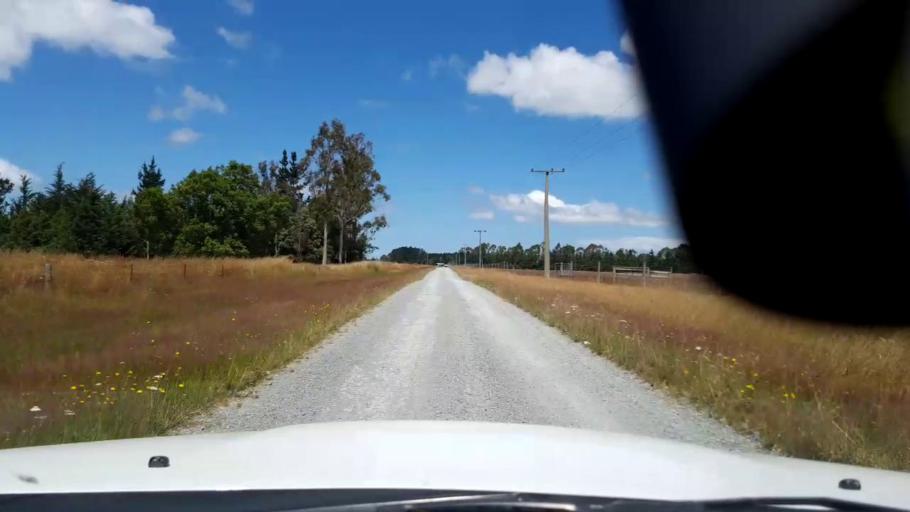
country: NZ
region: Canterbury
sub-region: Timaru District
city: Pleasant Point
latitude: -43.9872
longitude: 171.2900
